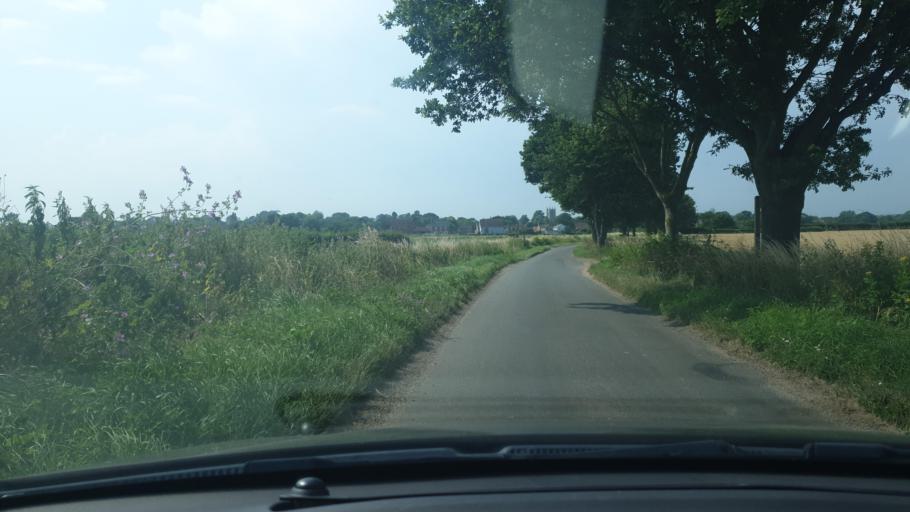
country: GB
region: England
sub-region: Suffolk
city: East Bergholt
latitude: 51.9542
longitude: 1.0048
